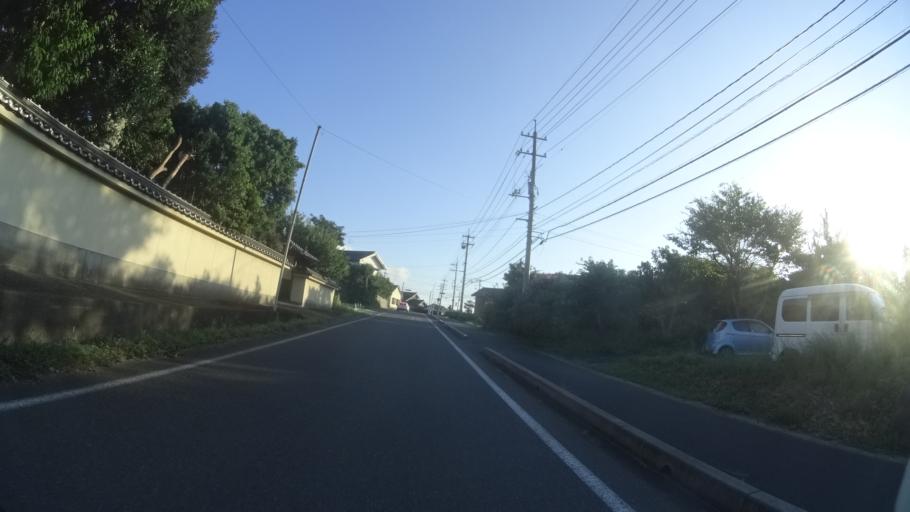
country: JP
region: Tottori
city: Yonago
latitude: 35.5071
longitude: 133.4985
